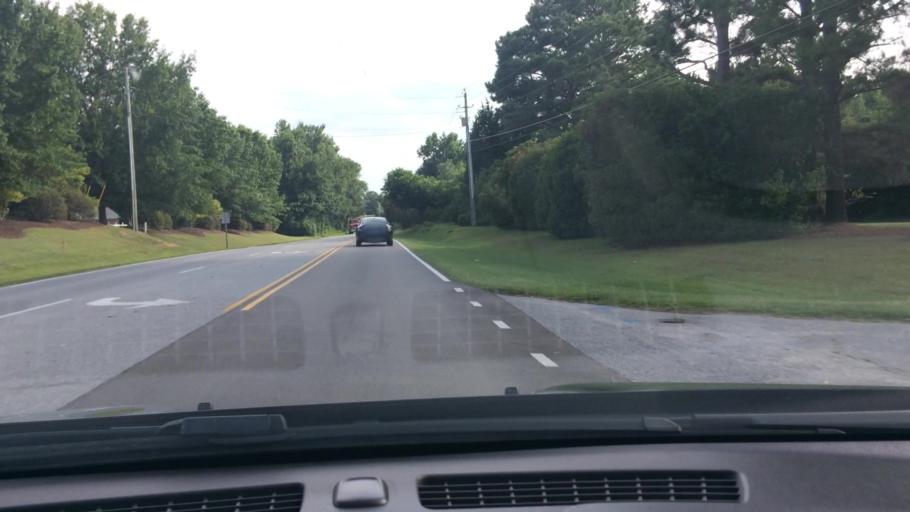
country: US
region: North Carolina
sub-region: Pitt County
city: Winterville
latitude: 35.5446
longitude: -77.3838
